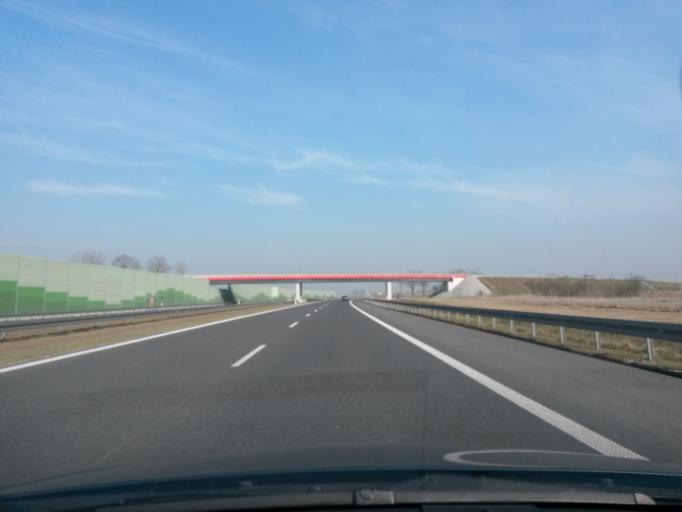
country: PL
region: Lodz Voivodeship
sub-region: Powiat kutnowski
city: Krzyzanow
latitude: 52.1464
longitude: 19.4820
